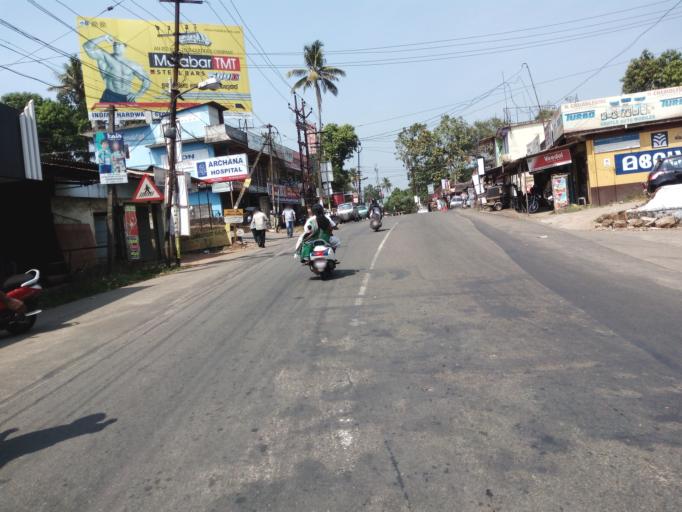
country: IN
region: Kerala
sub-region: Ernakulam
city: Muvattupula
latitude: 9.9029
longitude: 76.7113
